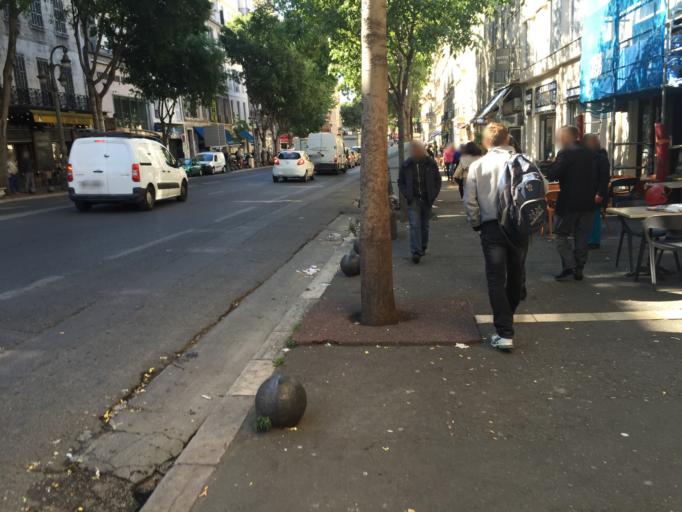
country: FR
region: Provence-Alpes-Cote d'Azur
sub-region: Departement des Bouches-du-Rhone
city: Marseille
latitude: 43.2989
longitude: 5.3808
